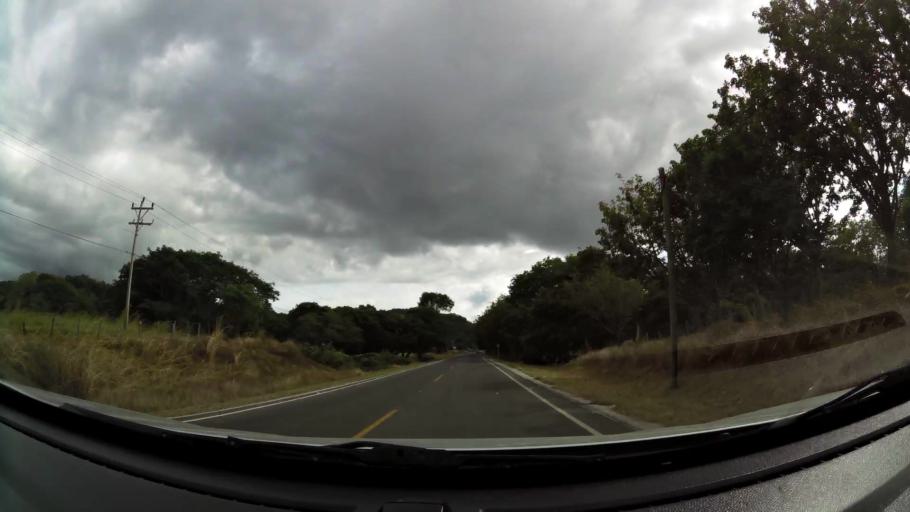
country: CR
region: Guanacaste
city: Nandayure
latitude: 10.2334
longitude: -85.2189
